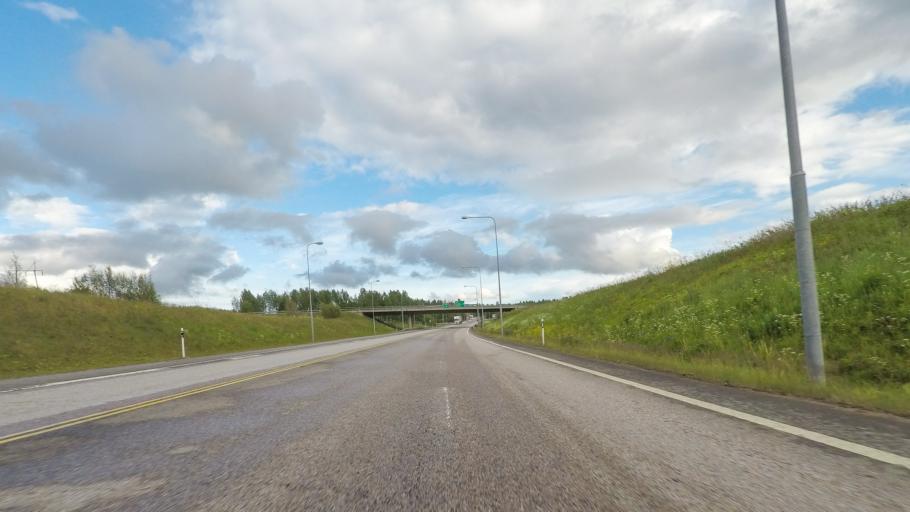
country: FI
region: Paijanne Tavastia
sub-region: Lahti
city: Heinola
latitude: 61.2982
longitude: 26.0674
